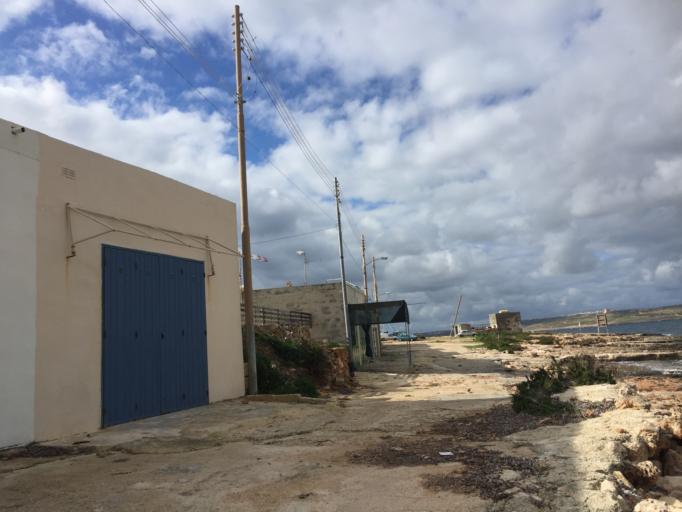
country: MT
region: Il-Mellieha
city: Mellieha
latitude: 35.9869
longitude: 14.3502
